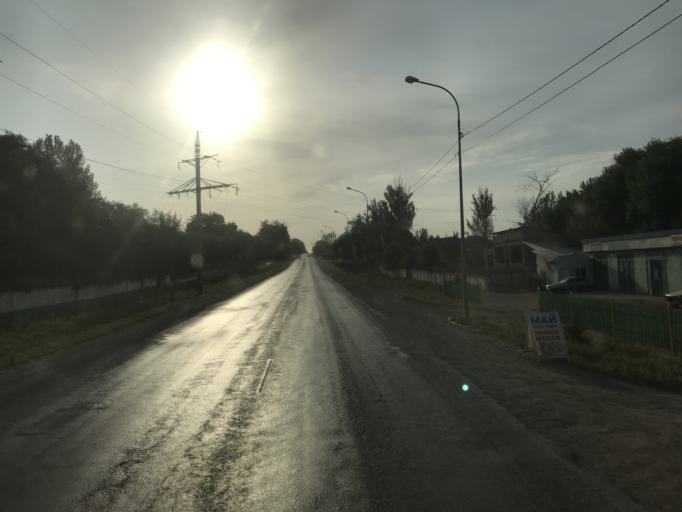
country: KZ
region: Ongtustik Qazaqstan
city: Saryaghash
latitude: 41.4901
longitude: 69.2654
